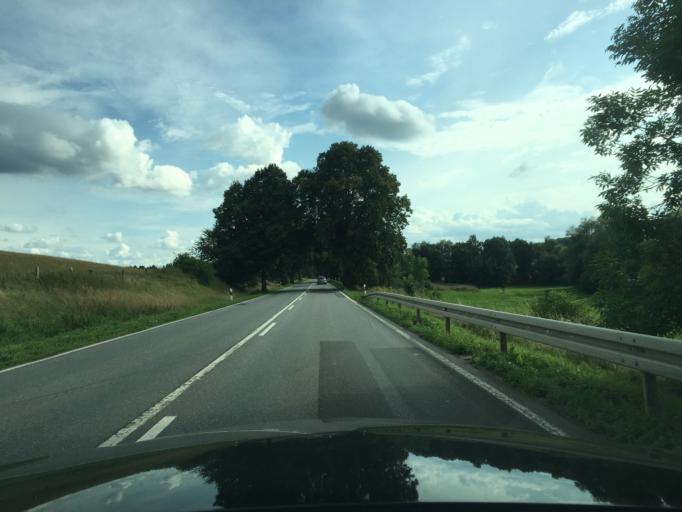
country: DE
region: Mecklenburg-Vorpommern
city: Penzlin
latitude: 53.4412
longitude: 13.0502
